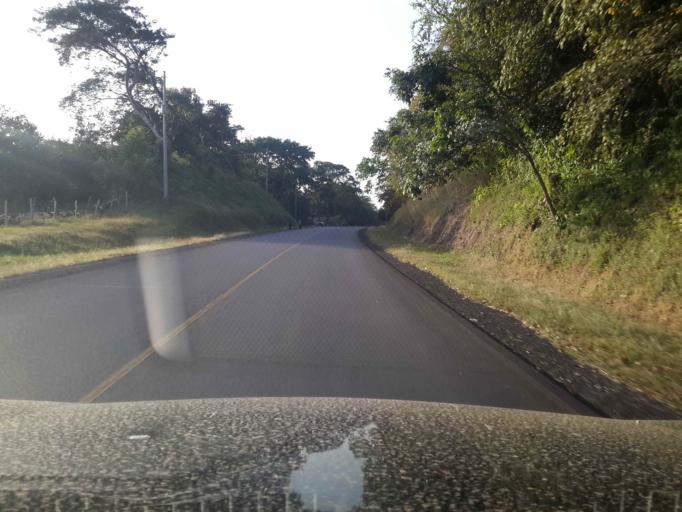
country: NI
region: Rio San Juan
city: San Miguelito
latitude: 11.3965
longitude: -84.8196
